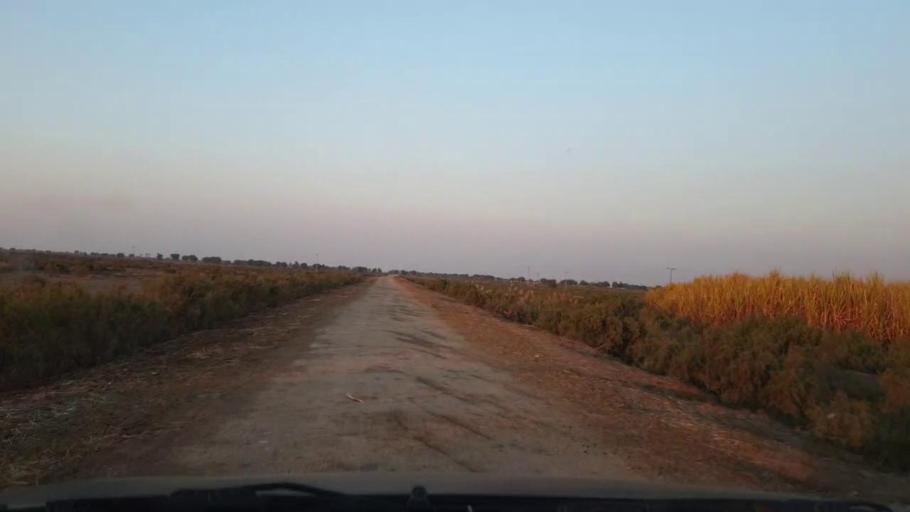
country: PK
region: Sindh
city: Jhol
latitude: 25.9277
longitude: 68.9662
